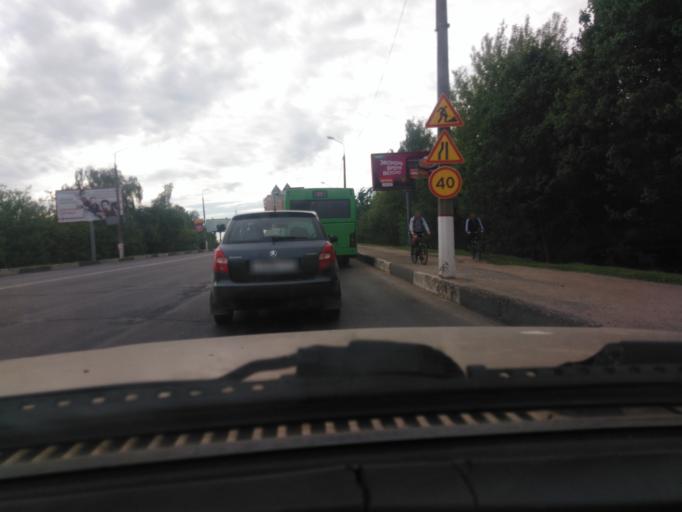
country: BY
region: Mogilev
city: Mahilyow
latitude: 53.9156
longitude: 30.3149
